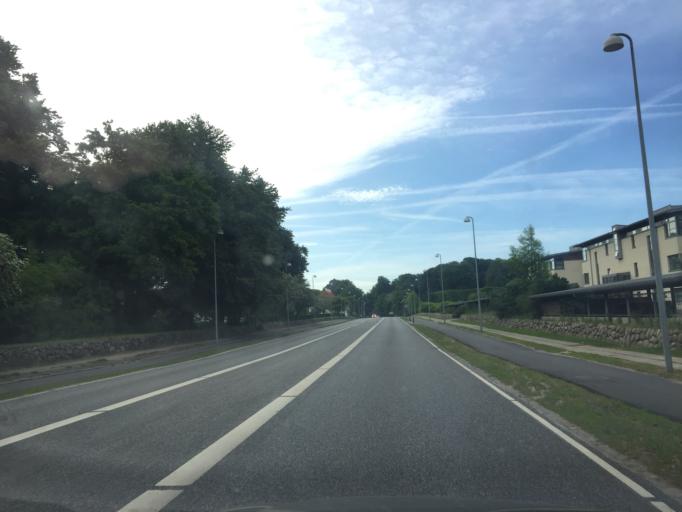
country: DK
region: Capital Region
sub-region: Lyngby-Tarbaek Kommune
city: Kongens Lyngby
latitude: 55.7814
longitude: 12.4922
